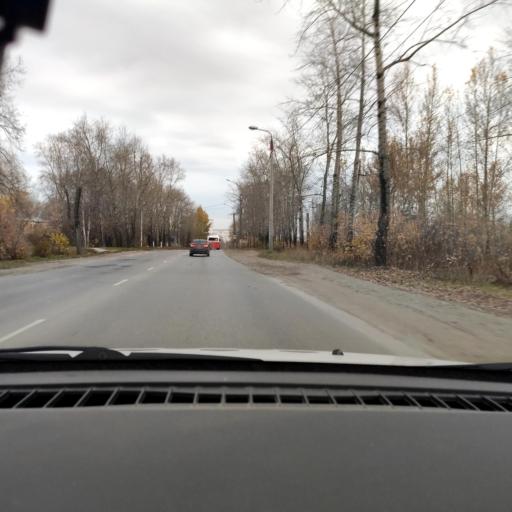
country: RU
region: Perm
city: Perm
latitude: 58.1207
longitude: 56.3689
